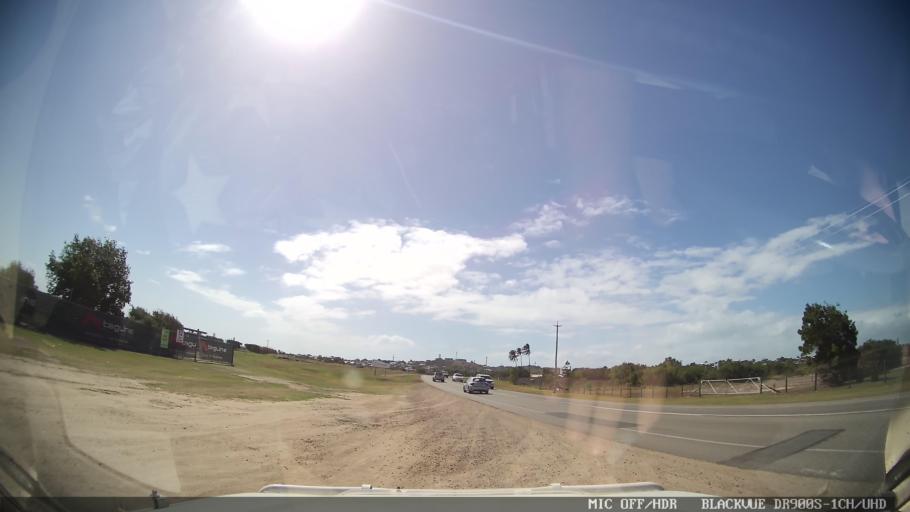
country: AU
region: Queensland
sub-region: Whitsunday
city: Bowen
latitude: -20.0125
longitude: 148.2249
